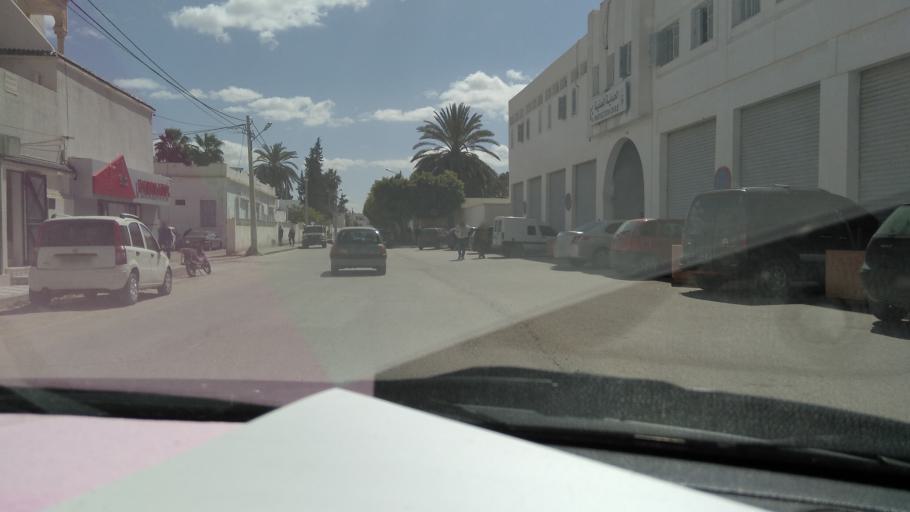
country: TN
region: Al Qayrawan
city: Kairouan
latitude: 35.6710
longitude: 10.1057
